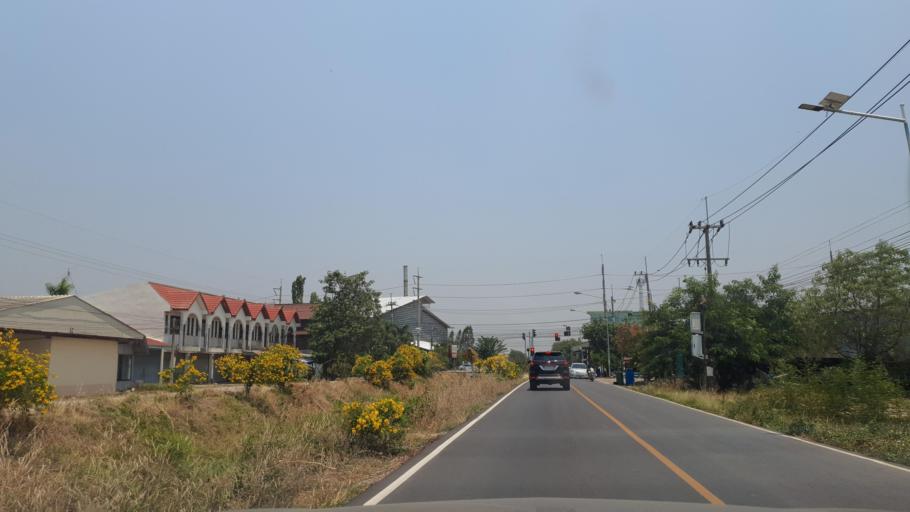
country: TH
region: Suphan Buri
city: Si Prachan
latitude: 14.6073
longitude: 100.1013
